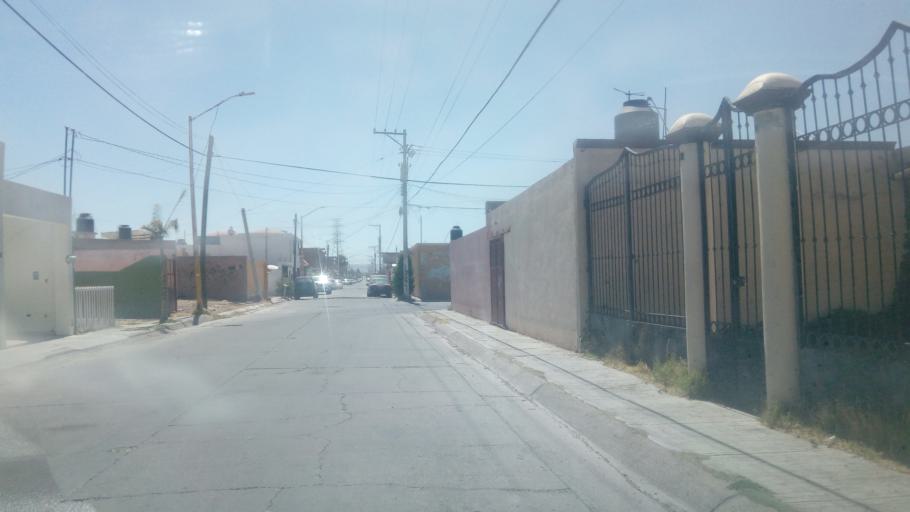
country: MX
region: Durango
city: Victoria de Durango
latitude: 24.0035
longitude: -104.6280
